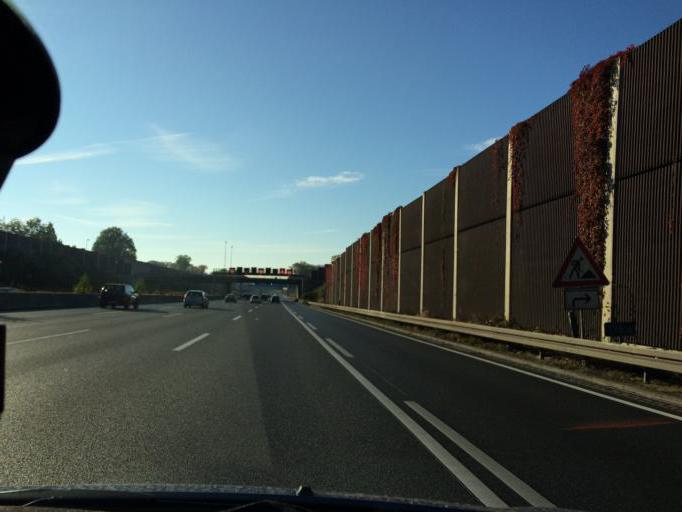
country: DE
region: North Rhine-Westphalia
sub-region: Regierungsbezirk Koln
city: Buchheim
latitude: 50.9685
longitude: 7.0304
